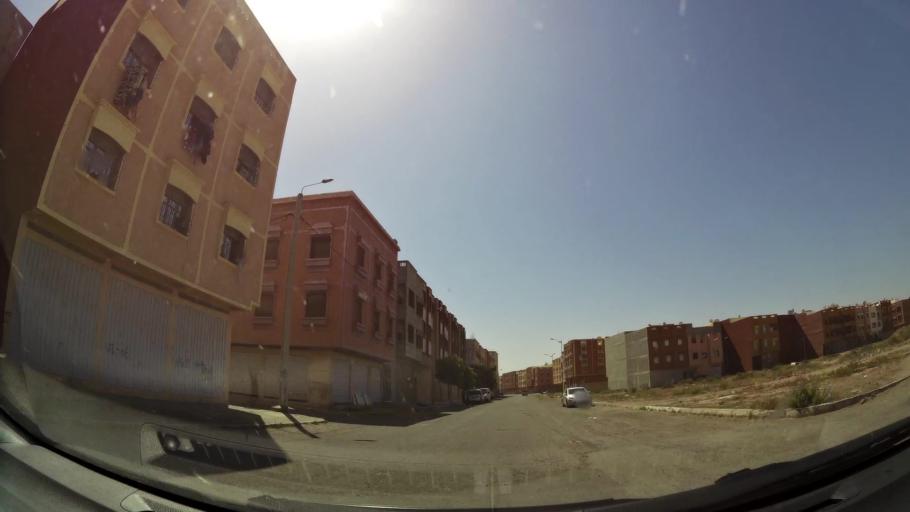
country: MA
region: Souss-Massa-Draa
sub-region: Inezgane-Ait Mellou
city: Inezgane
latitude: 30.3329
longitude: -9.5096
